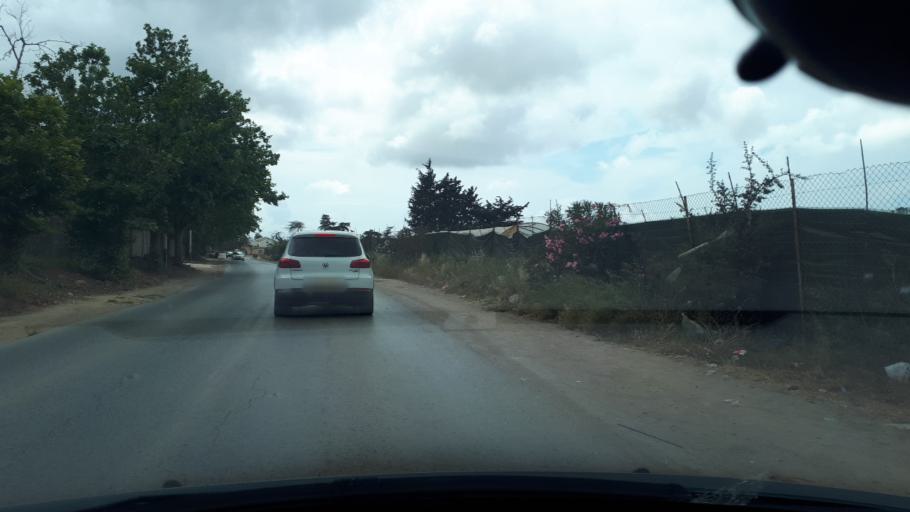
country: DZ
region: Tipaza
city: Cheraga
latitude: 36.7423
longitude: 2.9046
